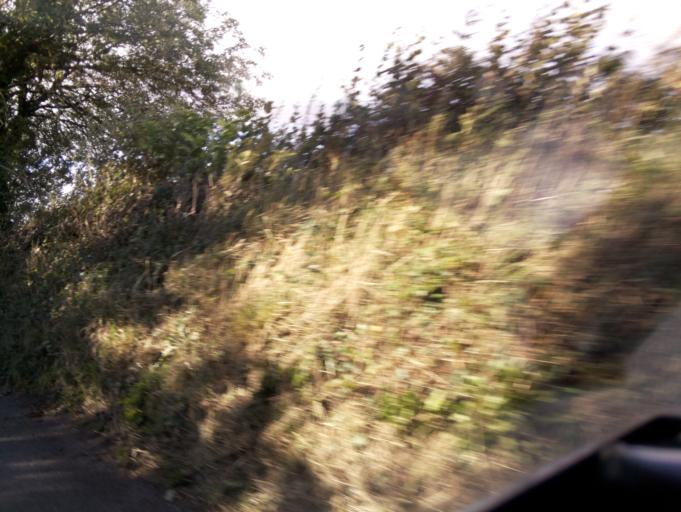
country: GB
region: England
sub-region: Devon
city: Totnes
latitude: 50.3580
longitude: -3.7297
